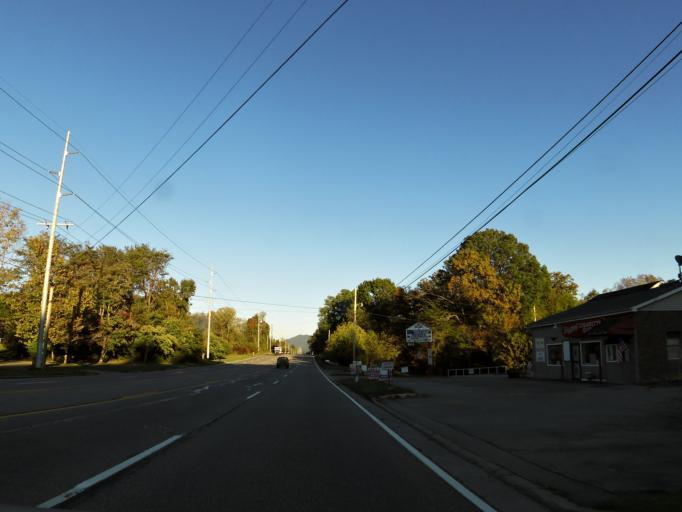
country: US
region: Tennessee
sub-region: Blount County
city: Eagleton Village
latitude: 35.7570
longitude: -83.9047
